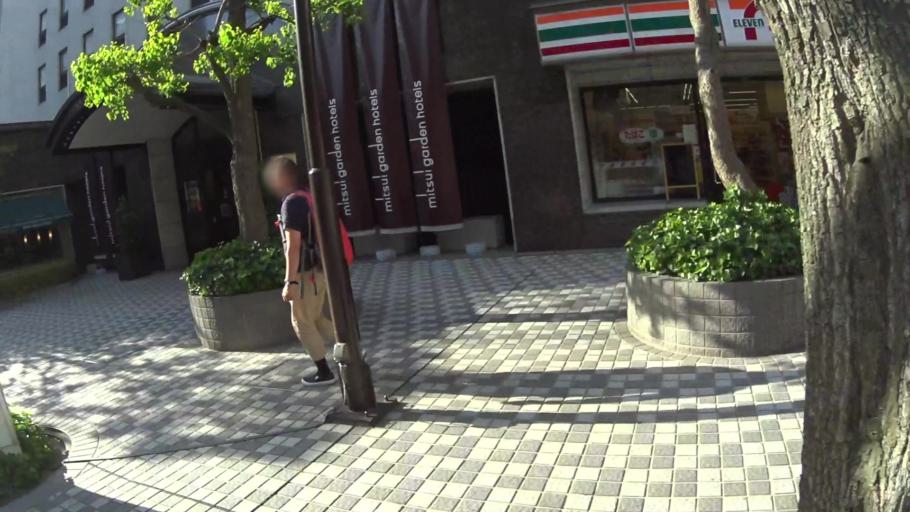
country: JP
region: Osaka
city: Osaka-shi
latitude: 34.6898
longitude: 135.5045
